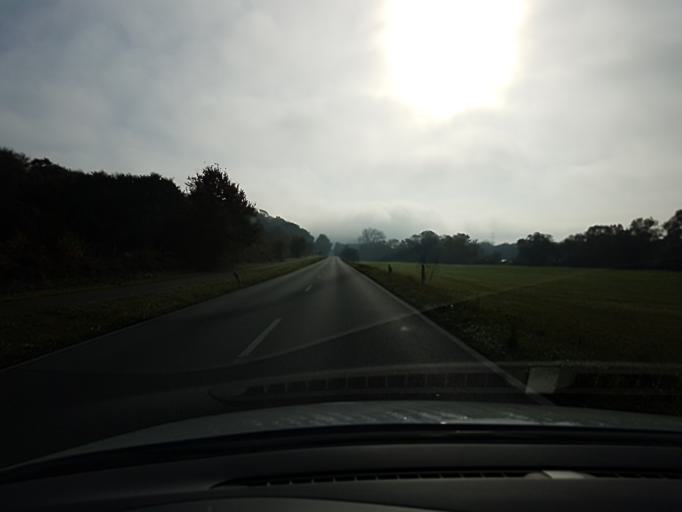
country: DE
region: Bavaria
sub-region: Regierungsbezirk Unterfranken
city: Sulzbach am Main
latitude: 49.8959
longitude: 9.1553
